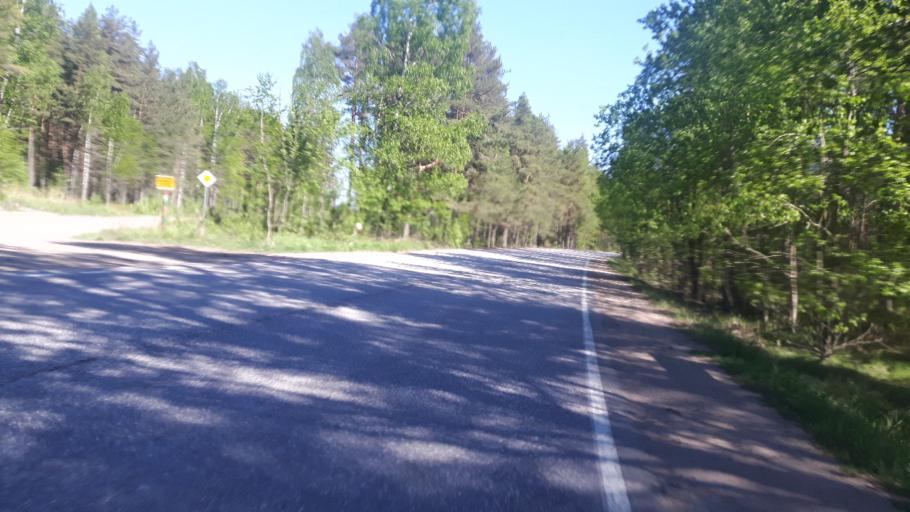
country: RU
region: Leningrad
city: Glebychevo
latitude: 60.2805
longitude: 28.8875
